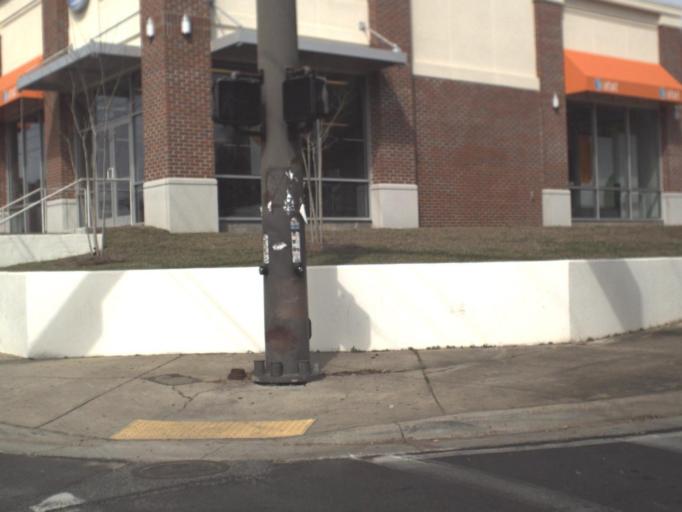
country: US
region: Florida
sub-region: Leon County
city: Tallahassee
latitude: 30.4492
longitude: -84.3099
